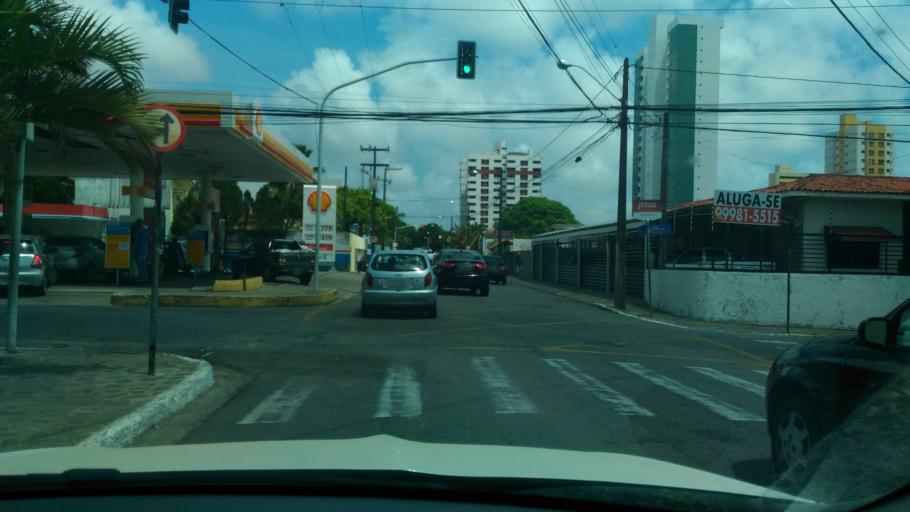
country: BR
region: Paraiba
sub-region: Joao Pessoa
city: Joao Pessoa
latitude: -7.1188
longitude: -34.8591
